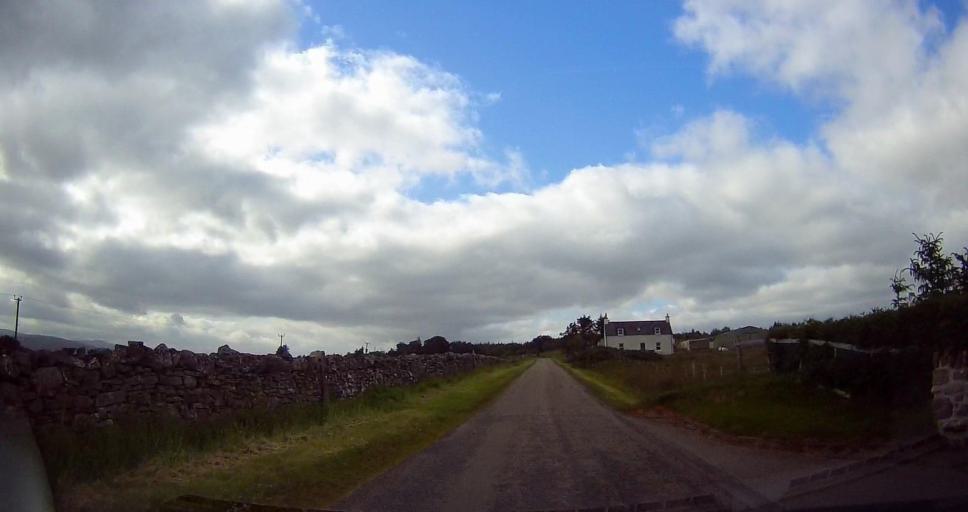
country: GB
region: Scotland
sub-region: Highland
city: Alness
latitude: 58.0782
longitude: -4.4452
